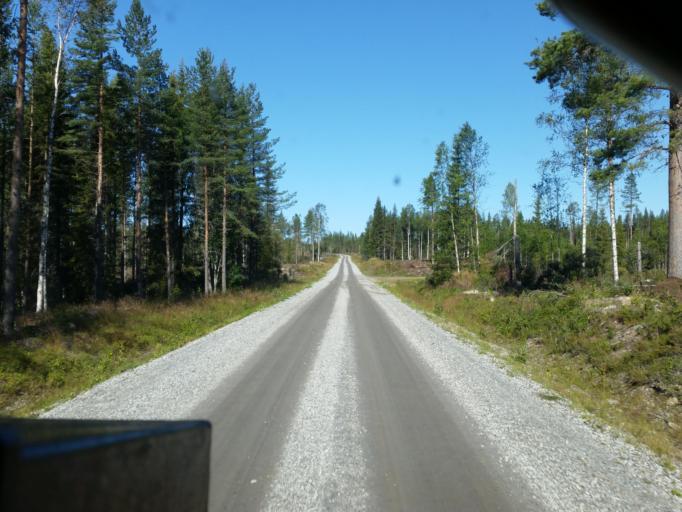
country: SE
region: Vaesterbotten
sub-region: Skelleftea Kommun
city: Storvik
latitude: 65.2317
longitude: 20.7689
